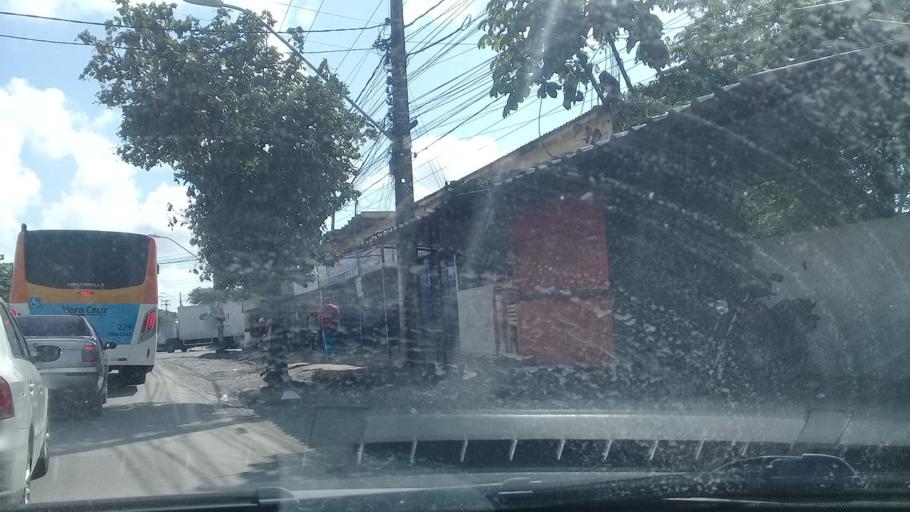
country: BR
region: Pernambuco
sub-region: Recife
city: Recife
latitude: -8.1095
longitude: -34.9357
